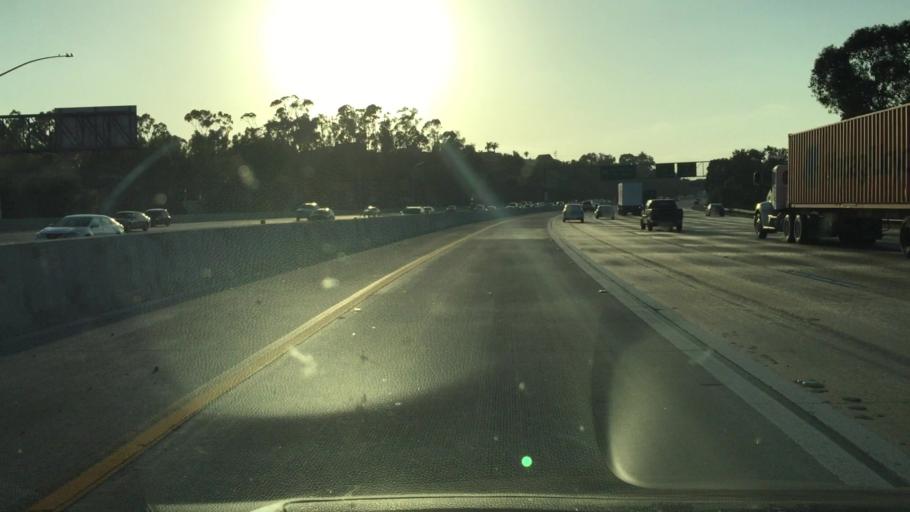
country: US
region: California
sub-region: San Diego County
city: Chula Vista
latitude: 32.6501
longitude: -117.0655
